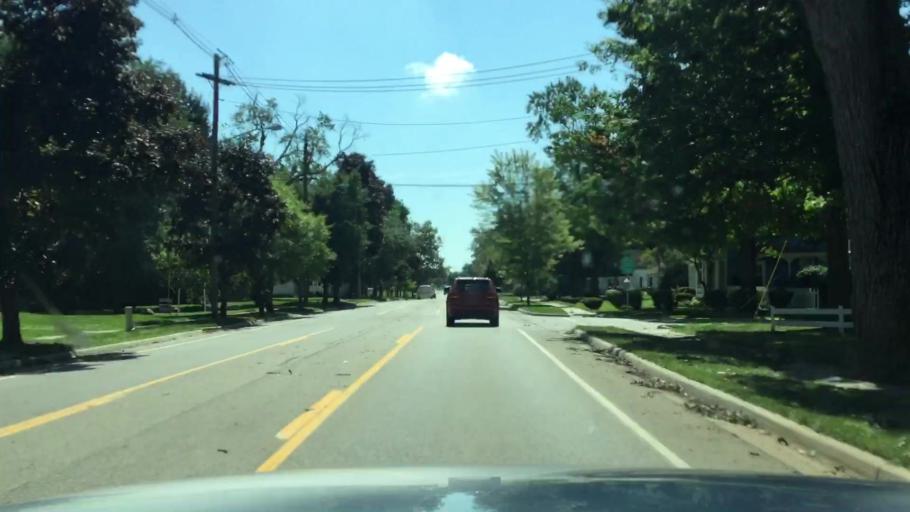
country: US
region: Michigan
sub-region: Lenawee County
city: Clinton
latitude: 42.0698
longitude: -83.9702
